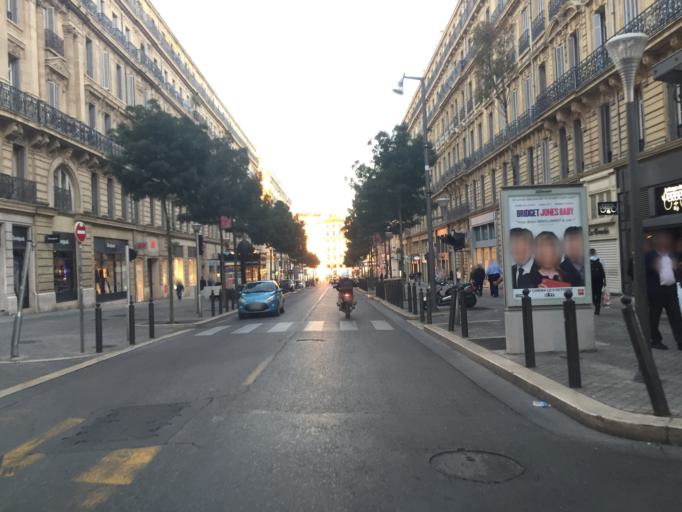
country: FR
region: Provence-Alpes-Cote d'Azur
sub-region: Departement des Bouches-du-Rhone
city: Marseille 02
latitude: 43.2978
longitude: 5.3729
